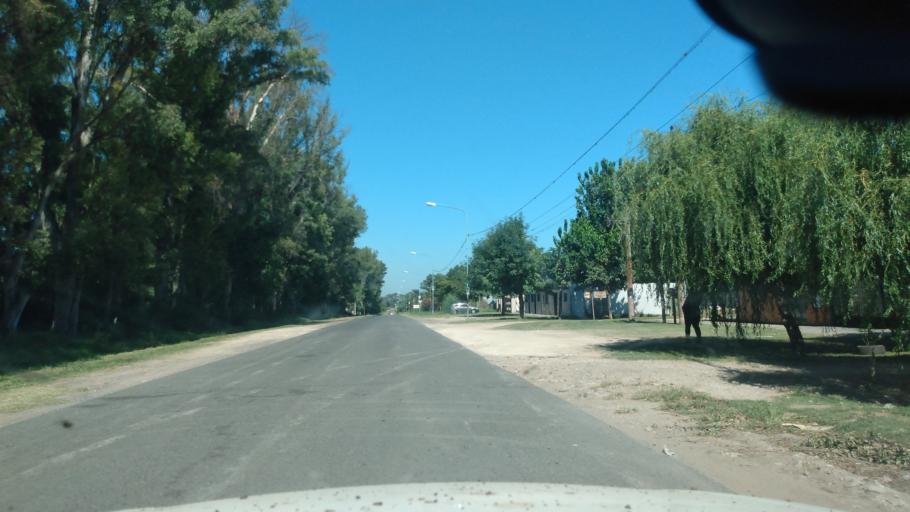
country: AR
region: Buenos Aires
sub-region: Partido de Lujan
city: Lujan
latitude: -34.5049
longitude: -59.0770
